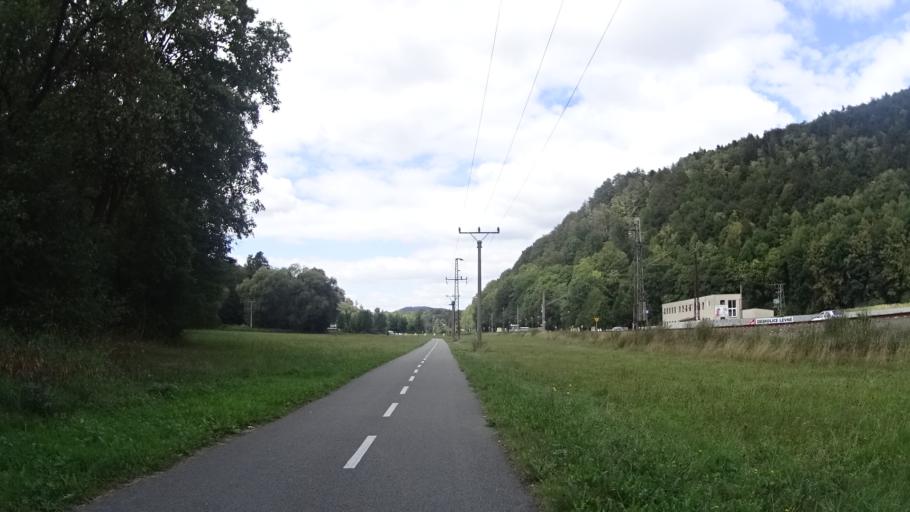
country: CZ
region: Pardubicky
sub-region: Okres Usti nad Orlici
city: Usti nad Orlici
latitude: 49.9867
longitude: 16.4308
